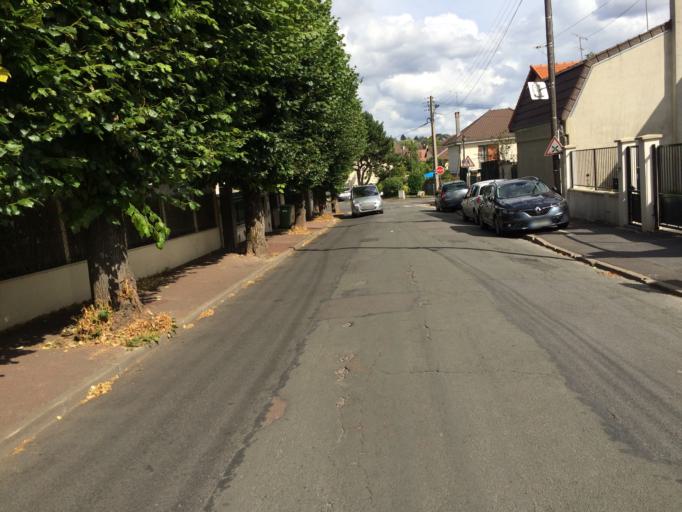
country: FR
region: Ile-de-France
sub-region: Departement de l'Essonne
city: Longjumeau
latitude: 48.6987
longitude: 2.3220
